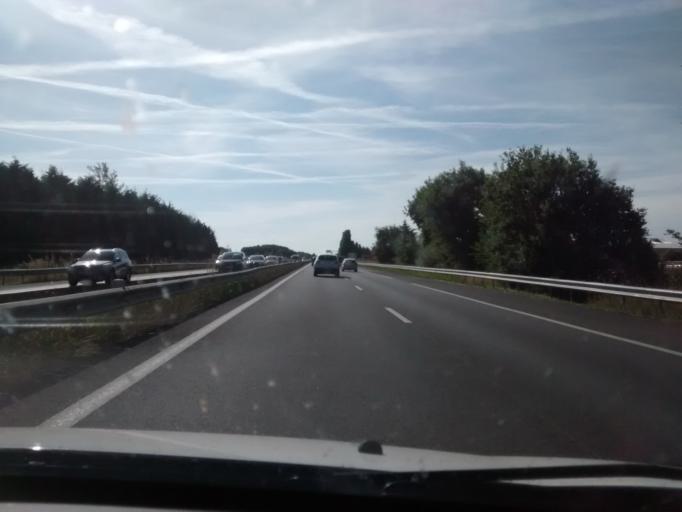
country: FR
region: Brittany
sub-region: Departement d'Ille-et-Vilaine
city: Chateaubourg
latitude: 48.0974
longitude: -1.4098
